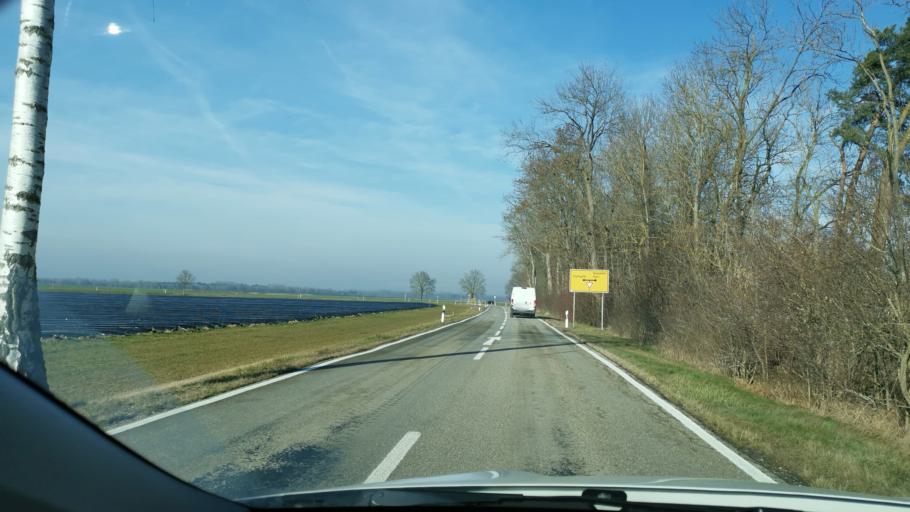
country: DE
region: Bavaria
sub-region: Swabia
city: Munster
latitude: 48.6401
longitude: 10.9215
